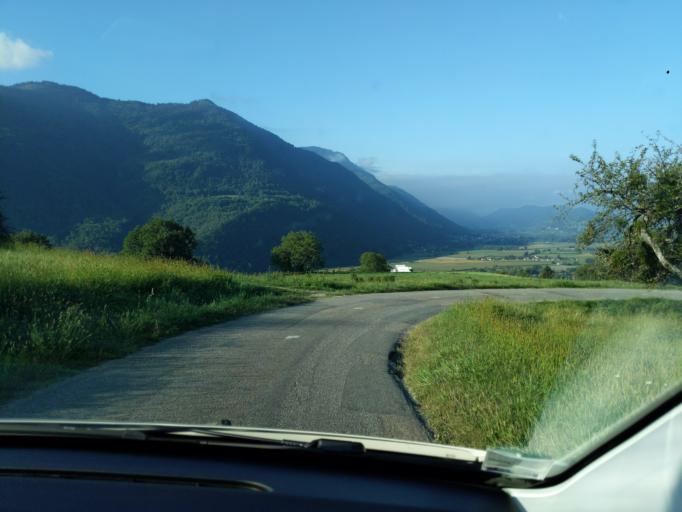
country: FR
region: Rhone-Alpes
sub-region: Departement de la Savoie
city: Aiton
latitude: 45.5645
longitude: 6.2603
